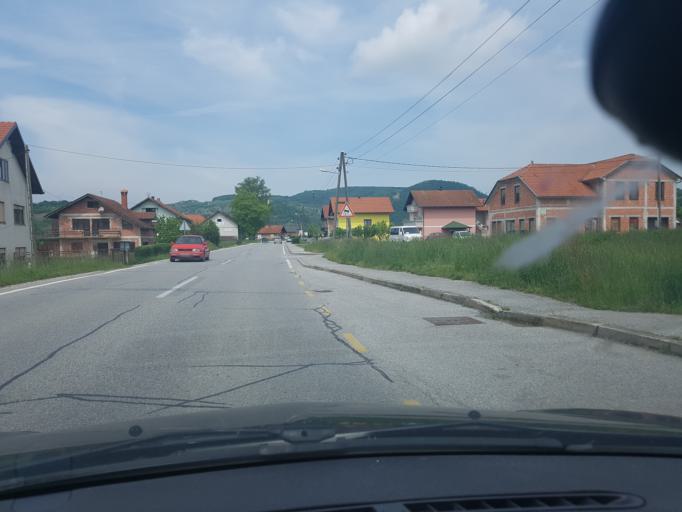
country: HR
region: Krapinsko-Zagorska
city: Pregrada
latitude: 46.1487
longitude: 15.7622
